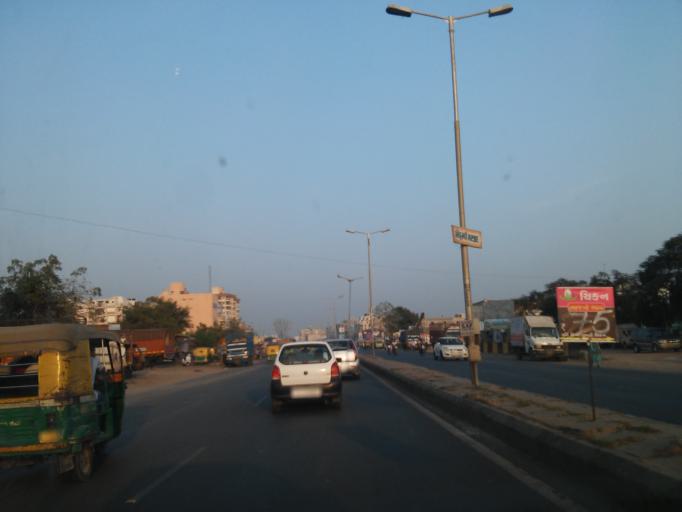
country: IN
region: Gujarat
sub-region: Ahmadabad
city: Sarkhej
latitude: 22.9885
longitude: 72.5091
